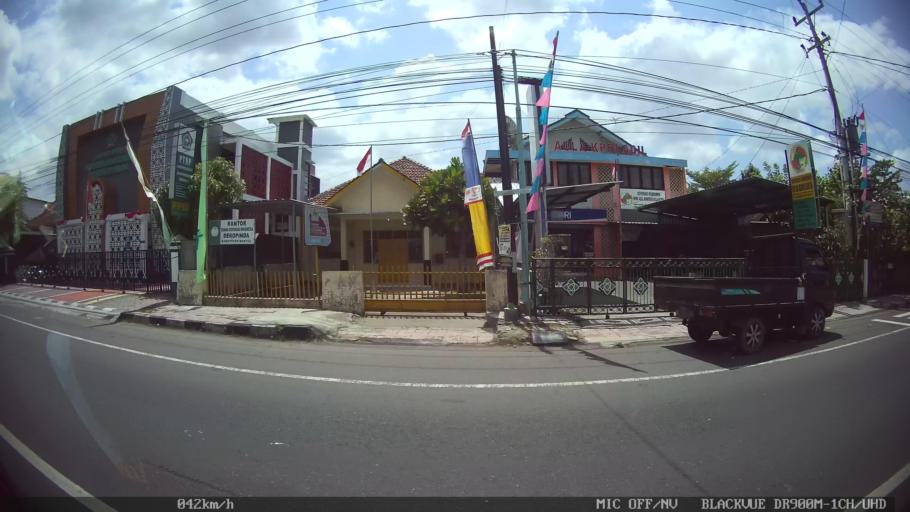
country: ID
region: Daerah Istimewa Yogyakarta
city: Bantul
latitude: -7.8930
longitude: 110.3369
